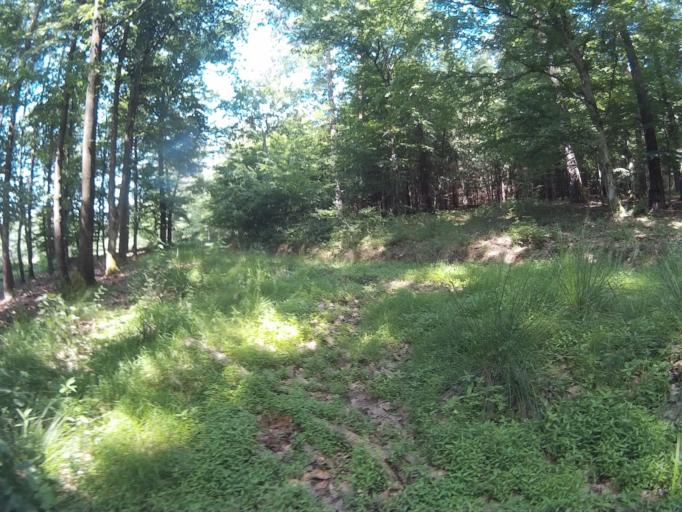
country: SI
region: Hodos-Hodos
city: Hodos
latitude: 46.8954
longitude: 16.4363
